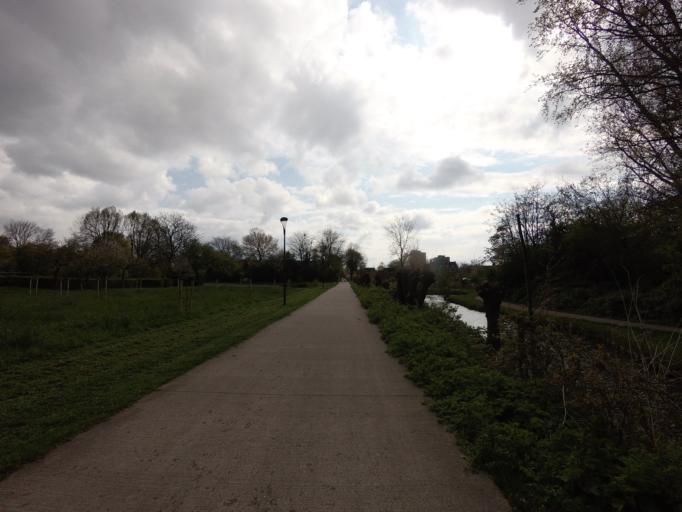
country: NL
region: Utrecht
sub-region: Gemeente Nieuwegein
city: Nieuwegein
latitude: 52.0398
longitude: 5.0876
